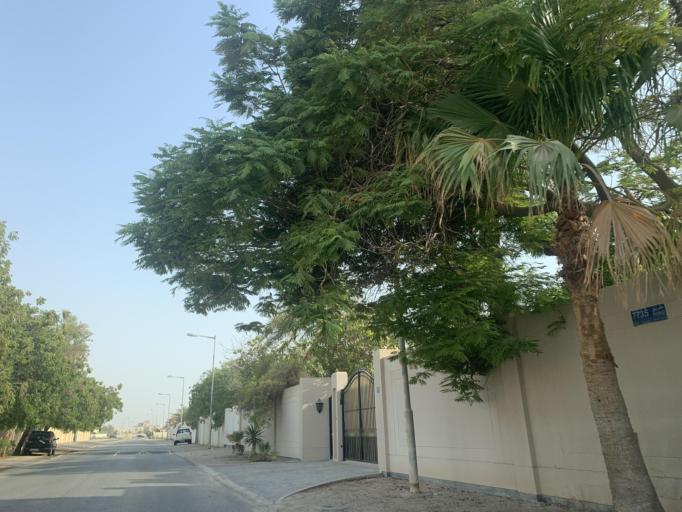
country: BH
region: Central Governorate
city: Madinat Hamad
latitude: 26.1768
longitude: 50.4740
